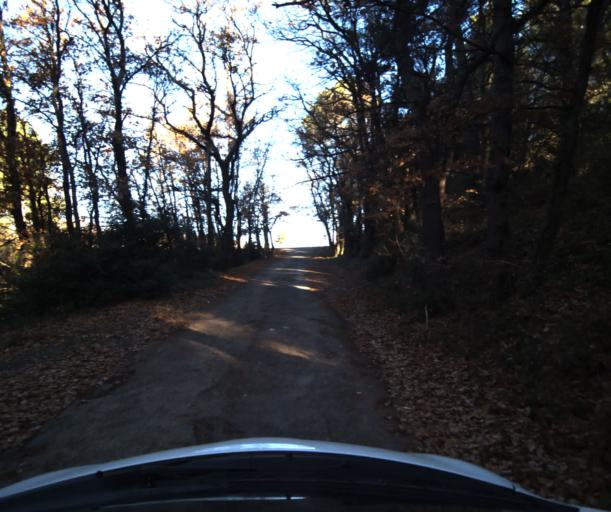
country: FR
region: Provence-Alpes-Cote d'Azur
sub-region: Departement du Vaucluse
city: Pertuis
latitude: 43.7169
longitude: 5.4962
